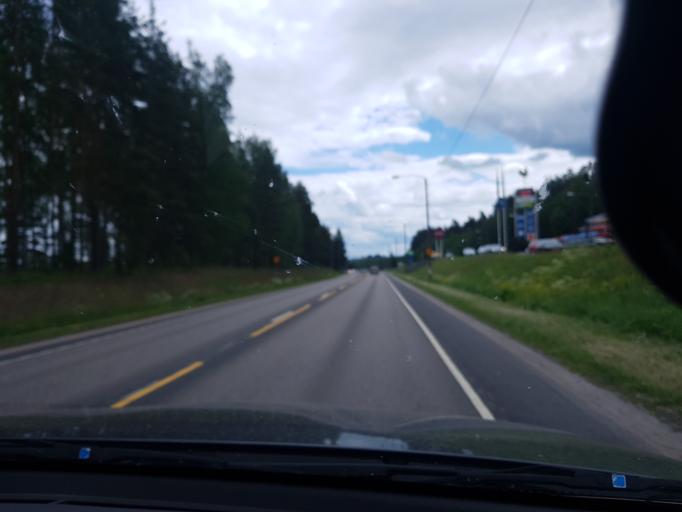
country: FI
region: Pirkanmaa
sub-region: Tampere
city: Paelkaene
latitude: 61.3484
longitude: 24.2567
